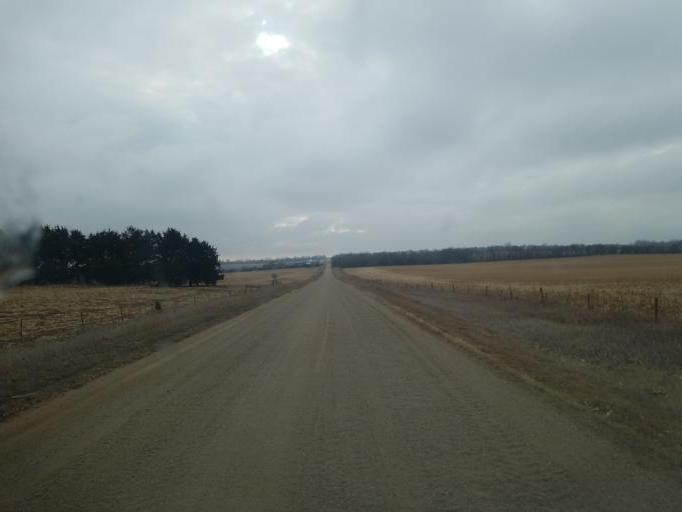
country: US
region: Nebraska
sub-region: Knox County
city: Creighton
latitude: 42.4652
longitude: -97.7984
